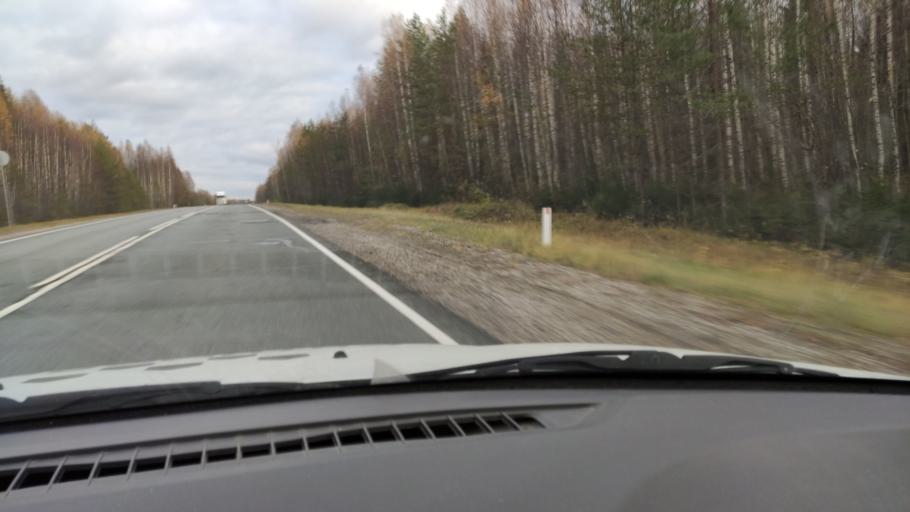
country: RU
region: Kirov
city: Dubrovka
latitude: 58.8994
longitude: 51.3062
